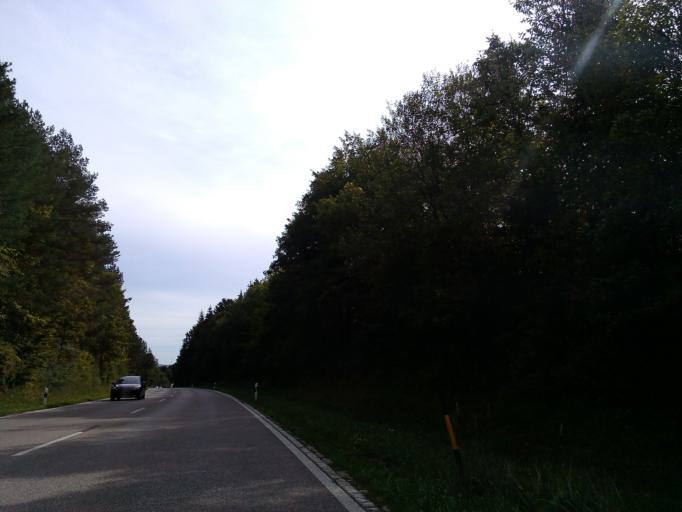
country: DE
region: Bavaria
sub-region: Upper Bavaria
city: Pocking
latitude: 47.9966
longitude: 11.3007
